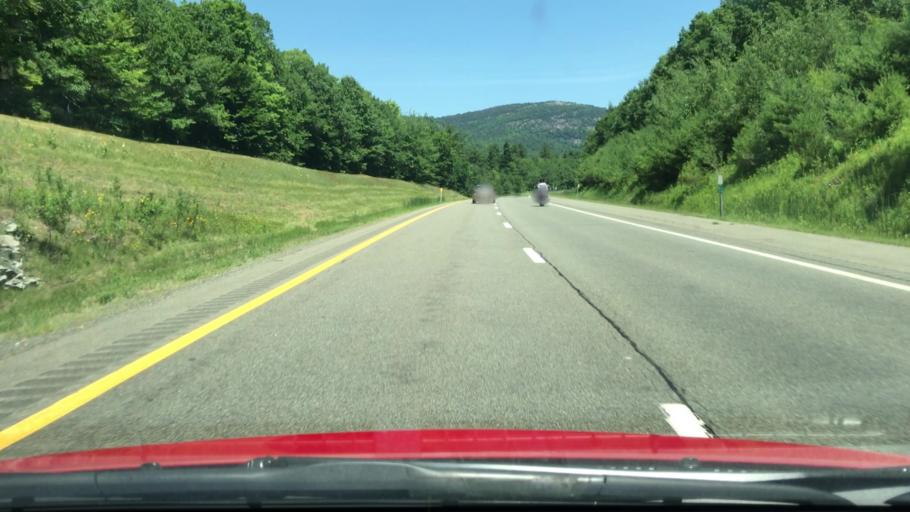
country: US
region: New York
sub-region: Essex County
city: Keeseville
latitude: 44.3667
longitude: -73.5290
